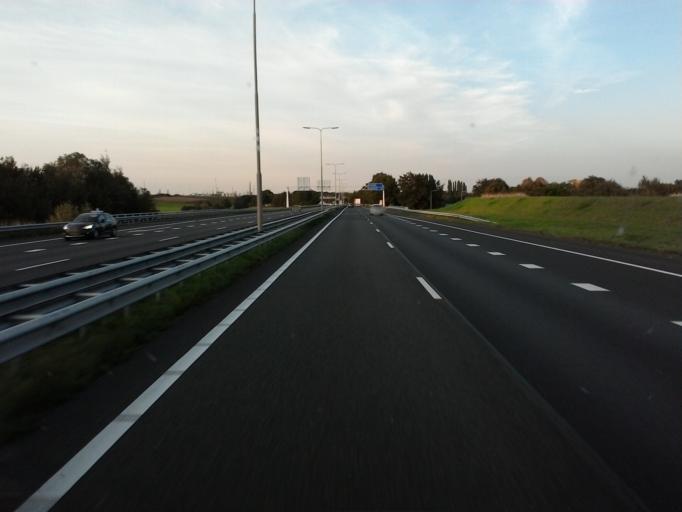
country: NL
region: Limburg
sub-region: Gemeente Beek
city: Beek
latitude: 50.9314
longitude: 5.7803
